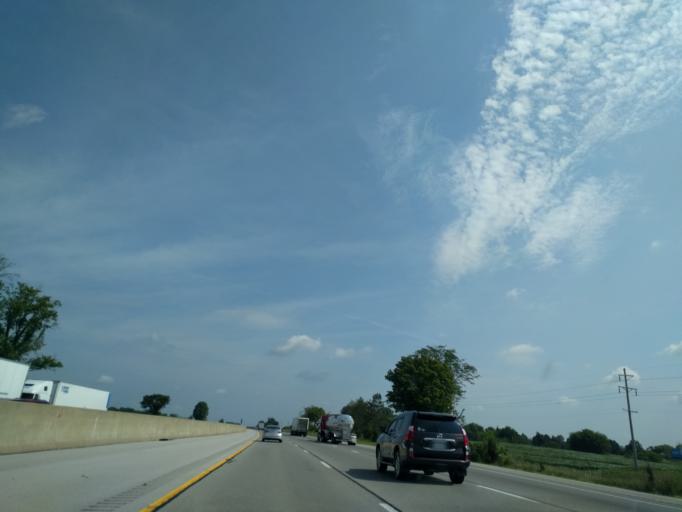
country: US
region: Kentucky
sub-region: Warren County
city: Plano
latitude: 36.8251
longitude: -86.4691
